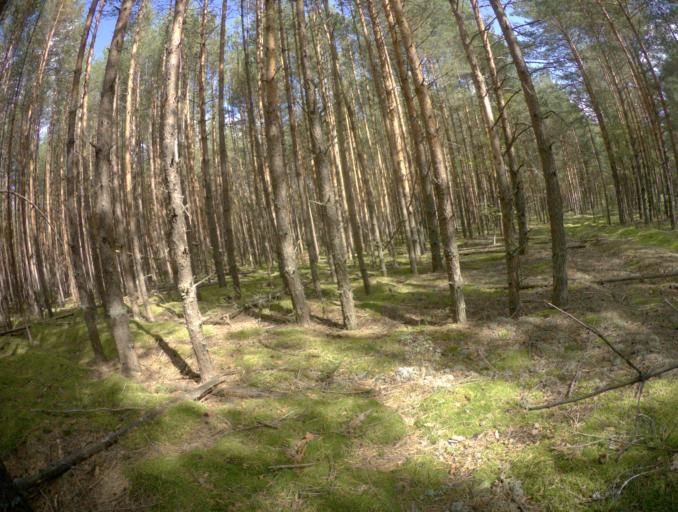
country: RU
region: Vladimir
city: Pokrov
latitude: 55.8465
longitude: 39.2447
